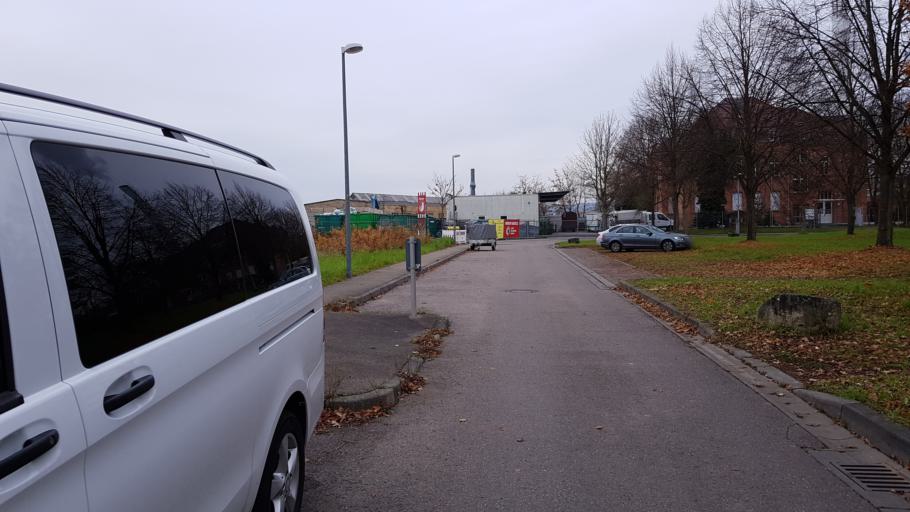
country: DE
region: Baden-Wuerttemberg
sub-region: Regierungsbezirk Stuttgart
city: Stuttgart Muehlhausen
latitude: 48.8187
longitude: 9.2167
